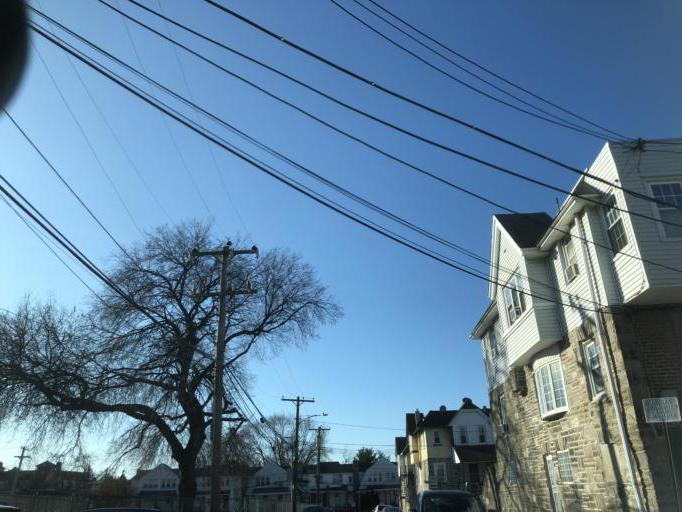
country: US
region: Pennsylvania
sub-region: Delaware County
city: East Lansdowne
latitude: 39.9569
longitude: -75.2682
